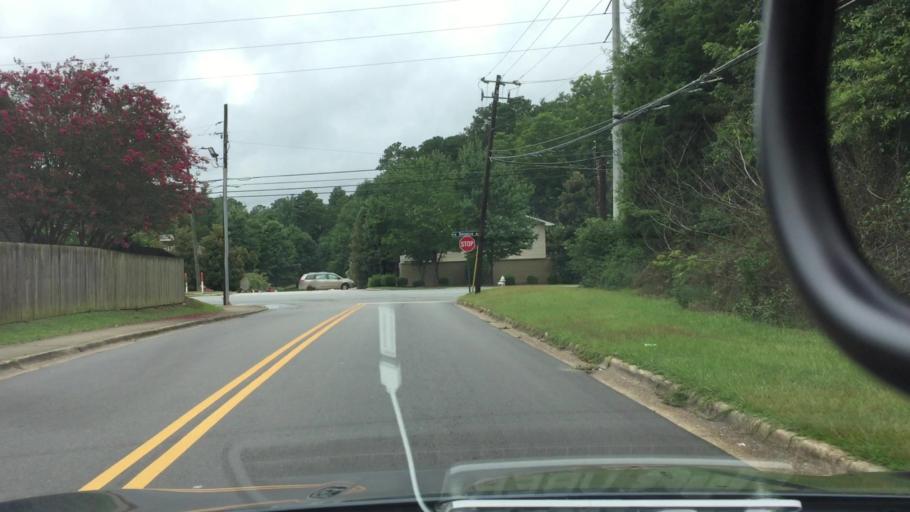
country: US
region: Alabama
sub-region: Lee County
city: Auburn
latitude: 32.6141
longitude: -85.4899
